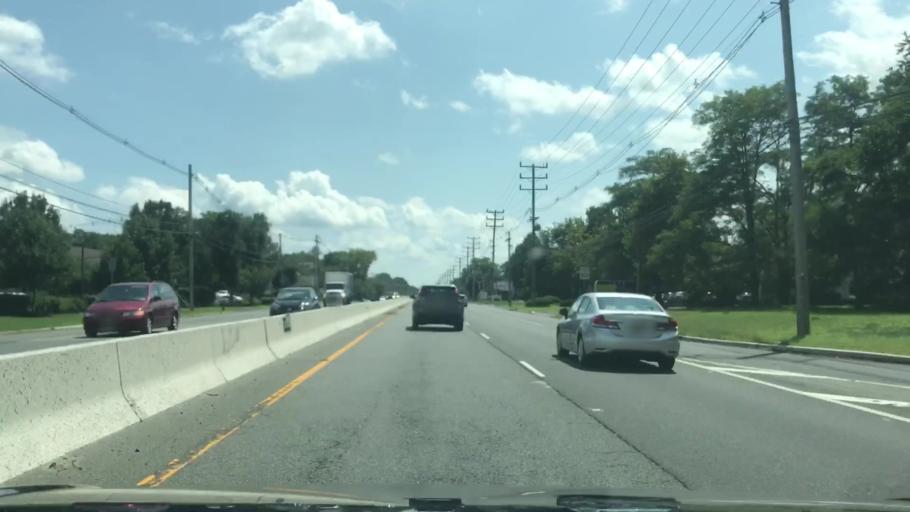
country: US
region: New Jersey
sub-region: Monmouth County
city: Oakhurst
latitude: 40.2621
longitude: -74.0415
